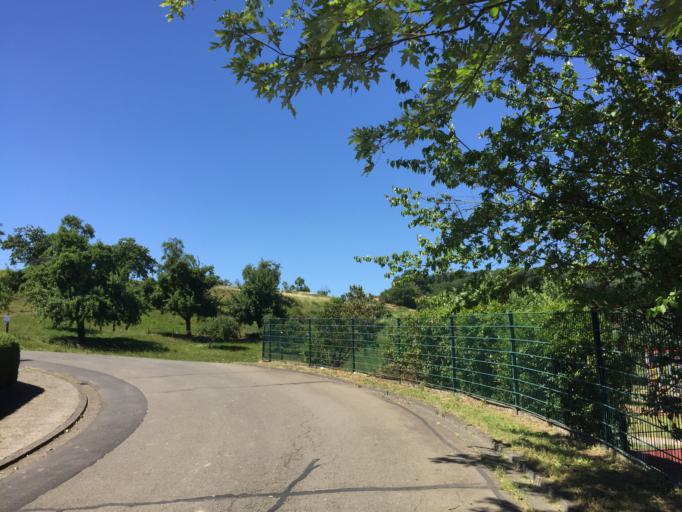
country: DE
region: Hesse
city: Beuern
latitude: 50.6279
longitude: 8.8135
